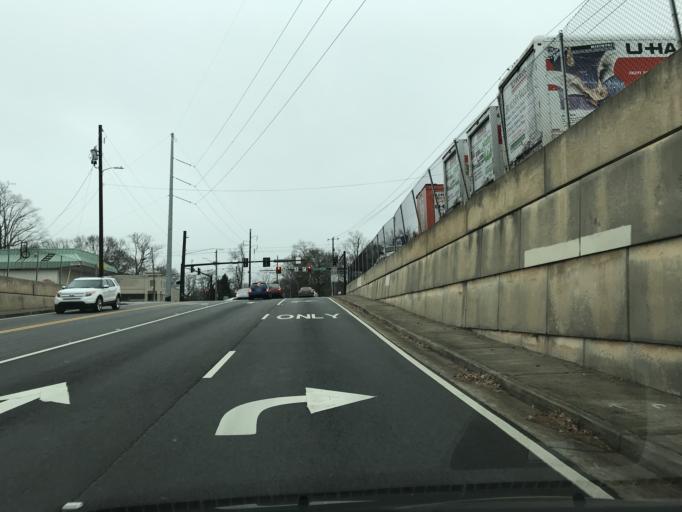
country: US
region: Georgia
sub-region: DeKalb County
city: Tucker
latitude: 33.8509
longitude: -84.2185
